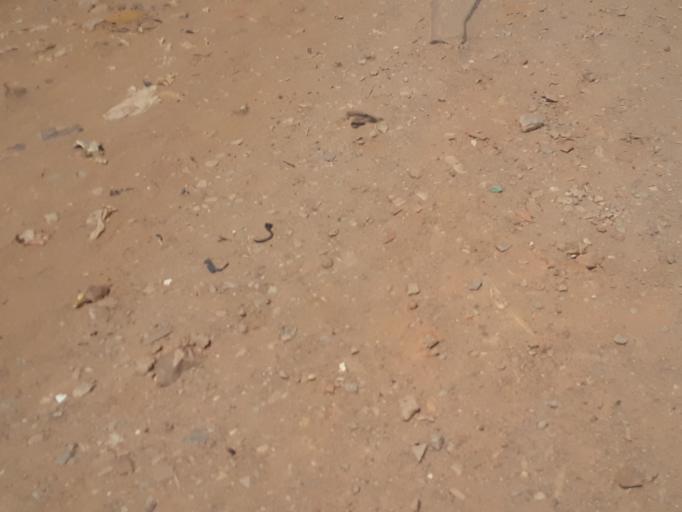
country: ZM
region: Lusaka
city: Lusaka
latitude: -15.3684
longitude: 28.2894
